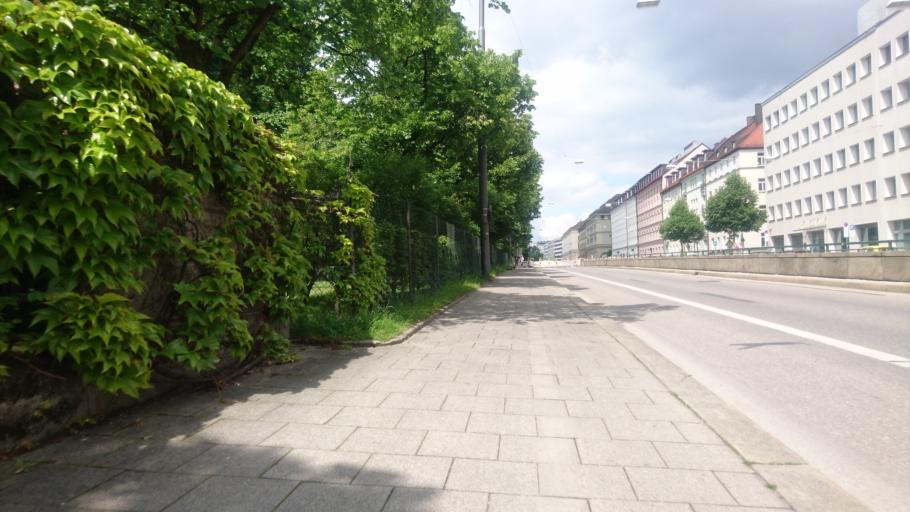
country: DE
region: Bavaria
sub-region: Upper Bavaria
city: Munich
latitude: 48.1445
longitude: 11.5824
